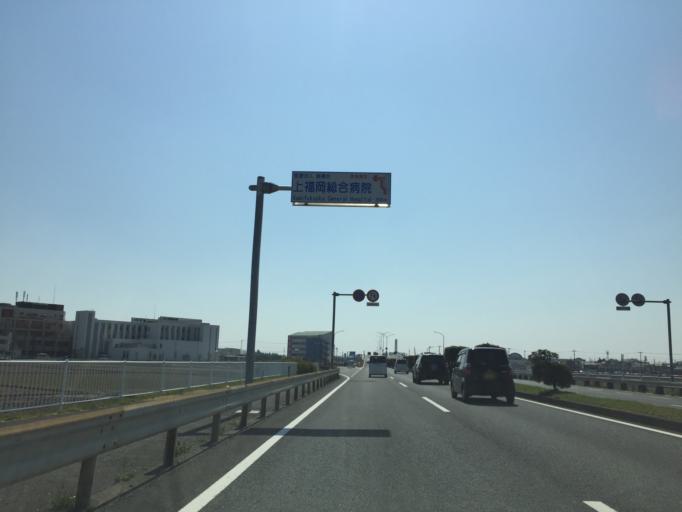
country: JP
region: Saitama
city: Kamifukuoka
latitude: 35.8786
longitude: 139.5368
